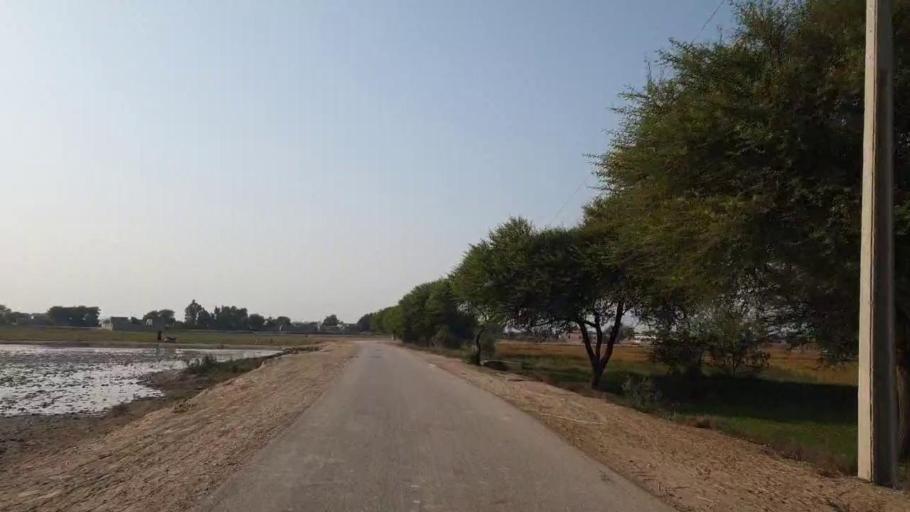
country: PK
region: Sindh
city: Bulri
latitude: 24.9966
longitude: 68.3807
